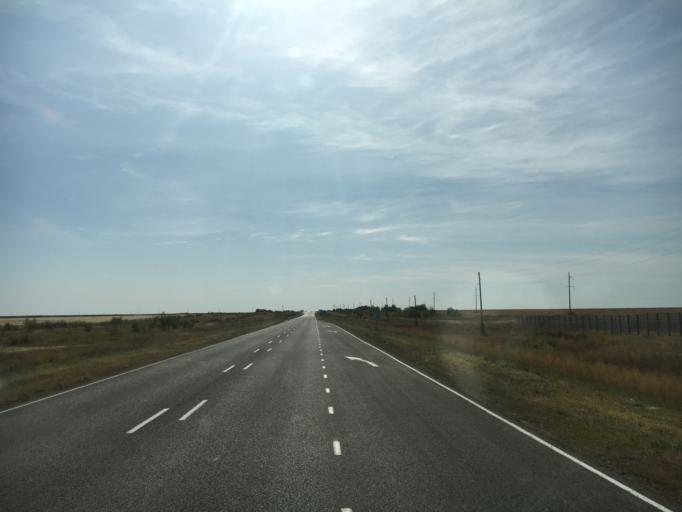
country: KZ
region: Batys Qazaqstan
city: Peremetnoe
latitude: 51.1325
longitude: 50.8996
